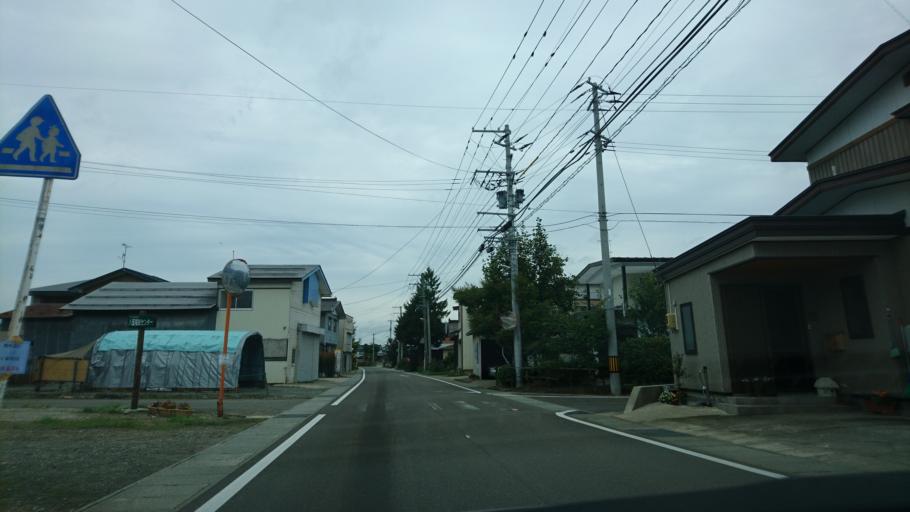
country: JP
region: Akita
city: Yuzawa
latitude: 39.1679
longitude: 140.5597
